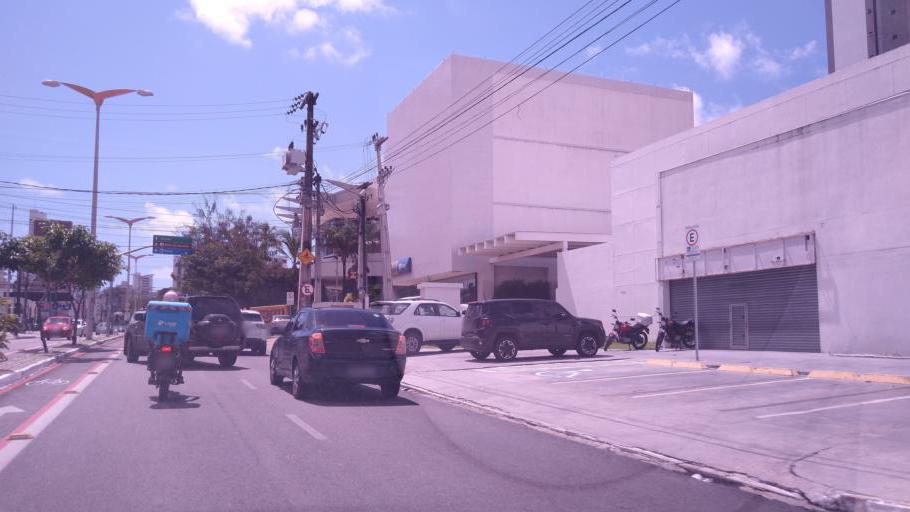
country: BR
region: Ceara
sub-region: Fortaleza
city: Fortaleza
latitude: -3.7358
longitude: -38.4928
